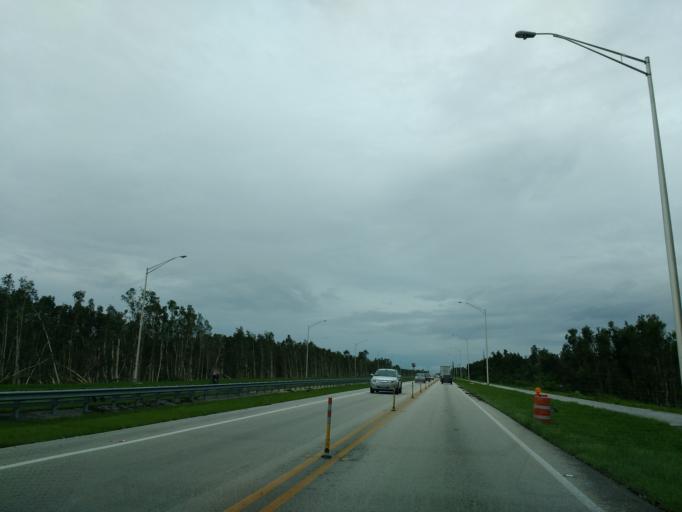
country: US
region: Florida
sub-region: Miami-Dade County
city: Kendall West
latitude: 25.7444
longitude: -80.4809
